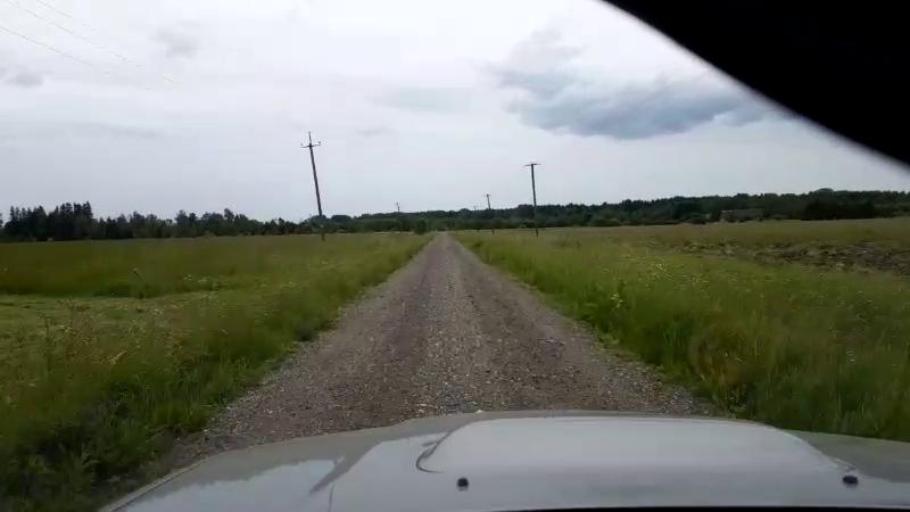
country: EE
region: Paernumaa
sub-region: Halinga vald
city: Parnu-Jaagupi
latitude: 58.5286
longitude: 24.6130
